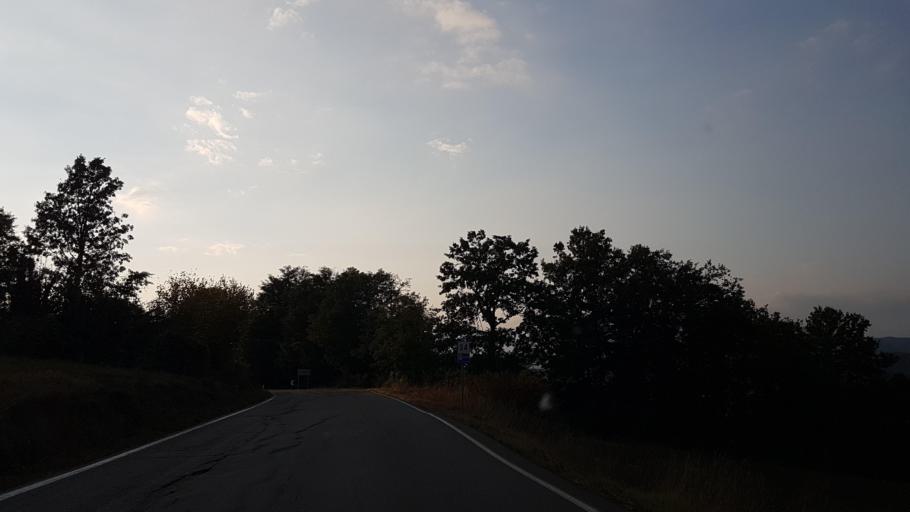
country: IT
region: Emilia-Romagna
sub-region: Provincia di Parma
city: Albareto
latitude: 44.4754
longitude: 9.7082
